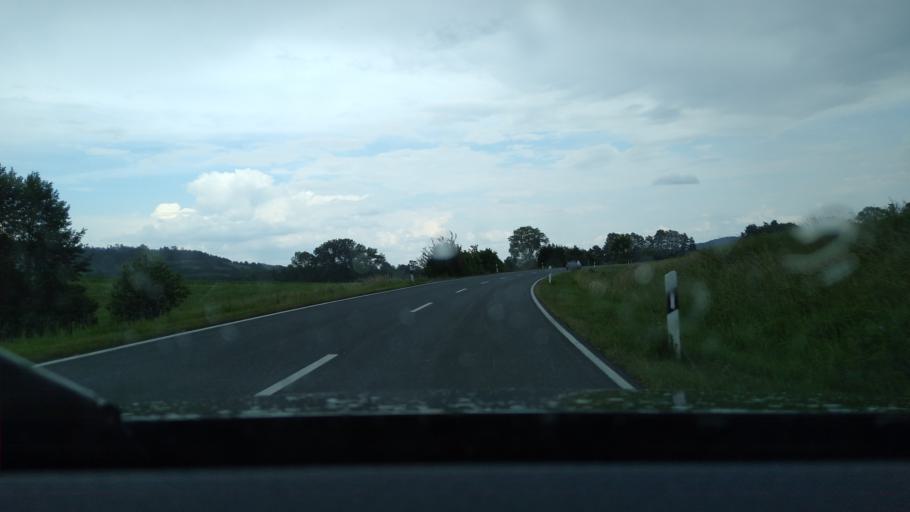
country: DE
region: Bavaria
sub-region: Regierungsbezirk Mittelfranken
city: Obernzenn
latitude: 49.4550
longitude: 10.4966
